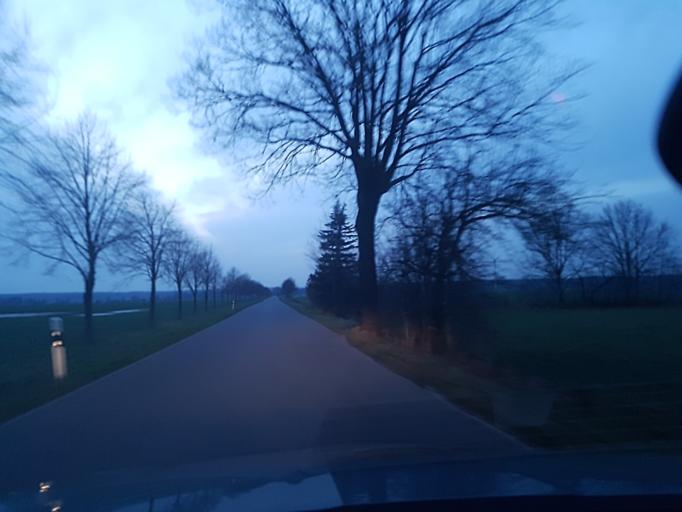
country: DE
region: Brandenburg
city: Ruckersdorf
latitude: 51.5919
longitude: 13.5285
